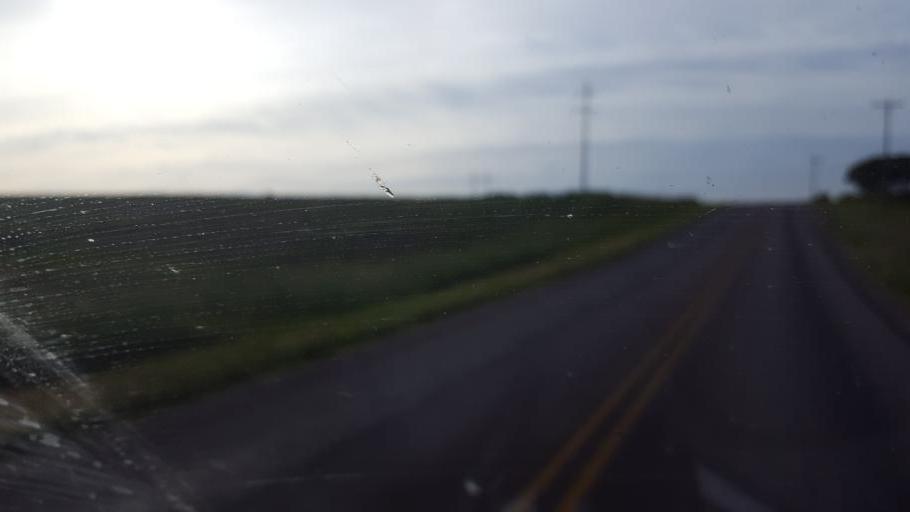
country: US
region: Wisconsin
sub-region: Vernon County
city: Hillsboro
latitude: 43.5943
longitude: -90.3961
